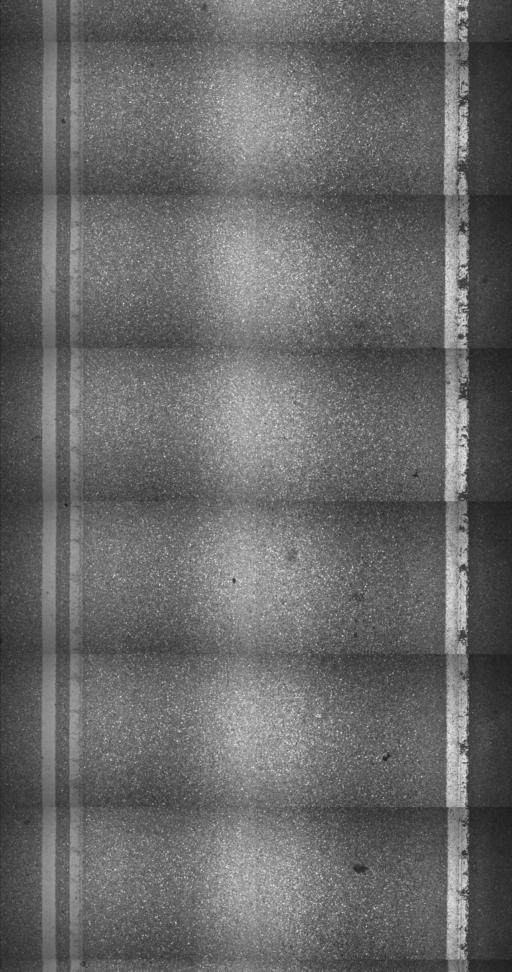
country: US
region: Vermont
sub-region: Addison County
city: Middlebury (village)
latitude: 43.9920
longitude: -73.1938
